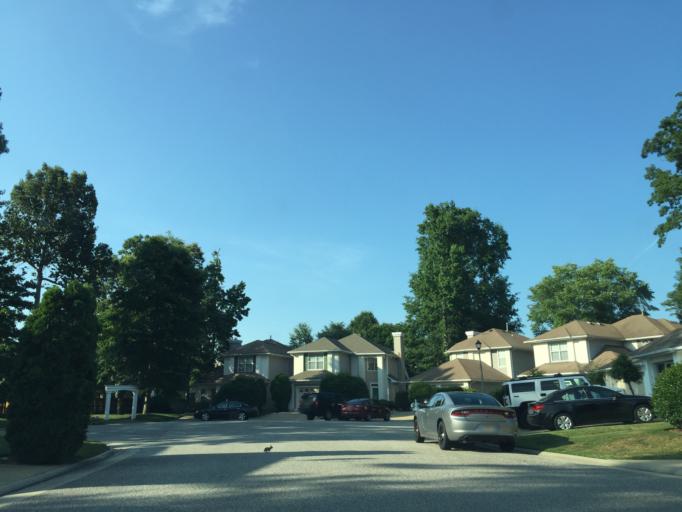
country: US
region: Virginia
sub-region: York County
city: Yorktown
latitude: 37.1172
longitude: -76.4789
